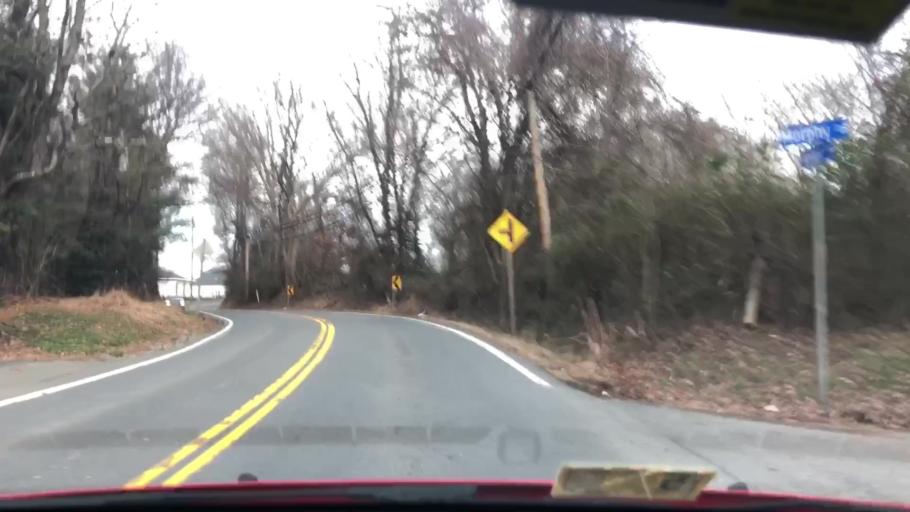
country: US
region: Virginia
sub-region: Fairfax County
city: Great Falls
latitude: 38.9809
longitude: -77.2934
